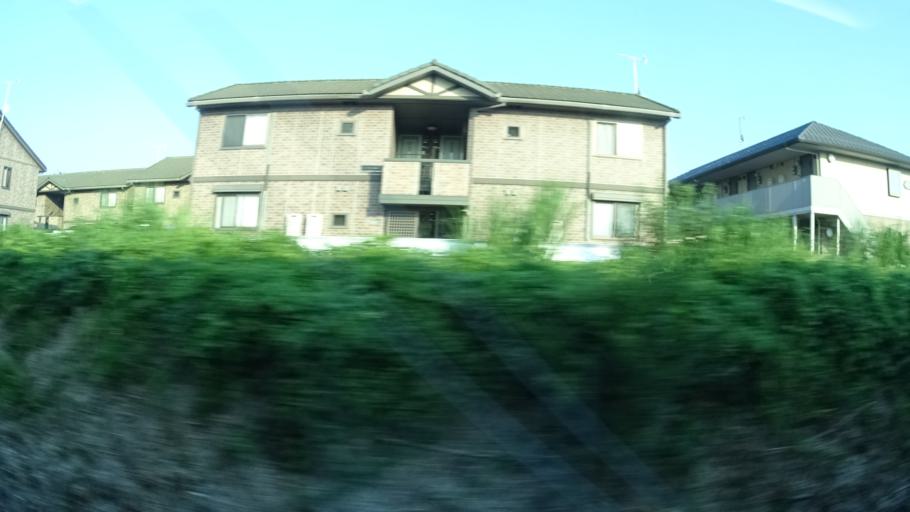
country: JP
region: Ibaraki
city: Funaishikawa
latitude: 36.4685
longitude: 140.5698
